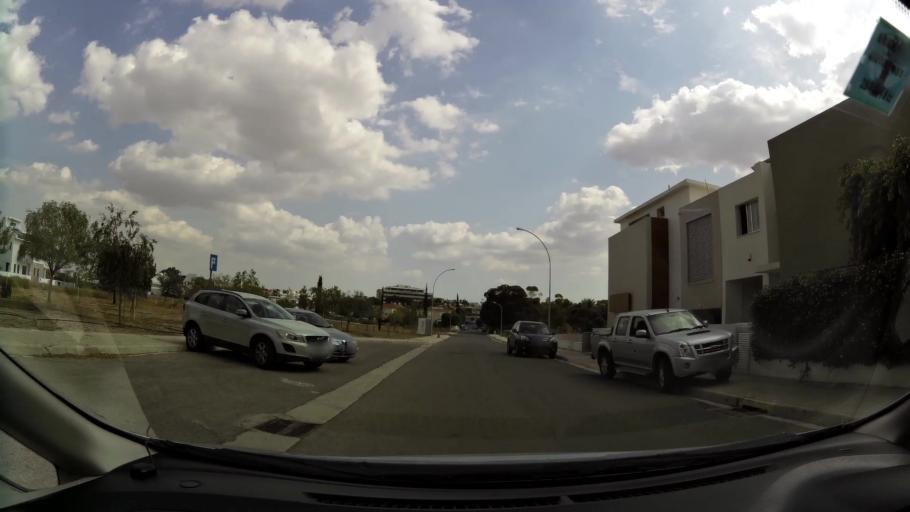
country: CY
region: Lefkosia
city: Geri
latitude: 35.1141
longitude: 33.3726
